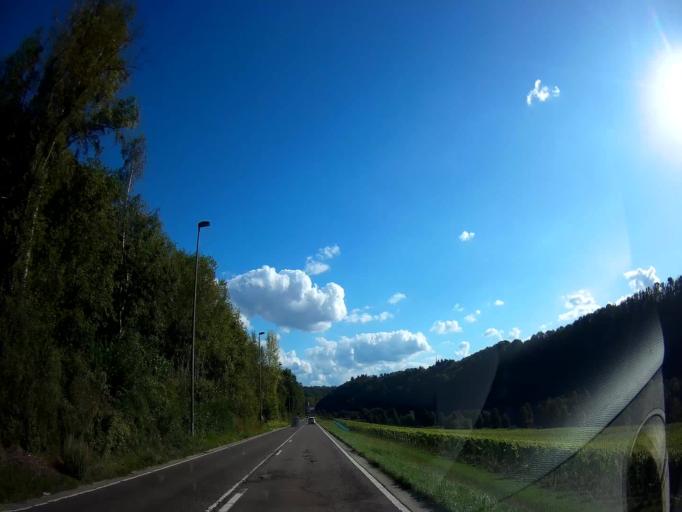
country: BE
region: Wallonia
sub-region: Province de Namur
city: Anhee
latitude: 50.2854
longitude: 4.8963
